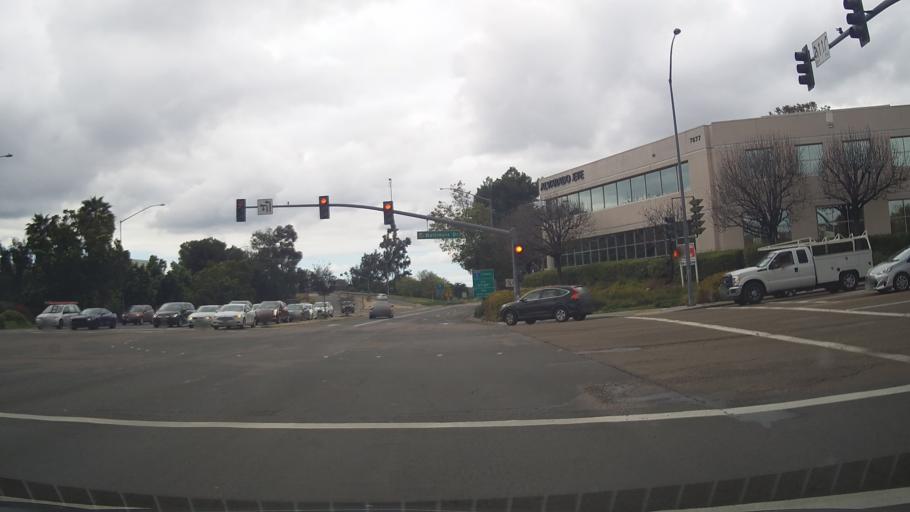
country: US
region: California
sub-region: San Diego County
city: La Mesa
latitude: 32.7741
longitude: -117.0271
